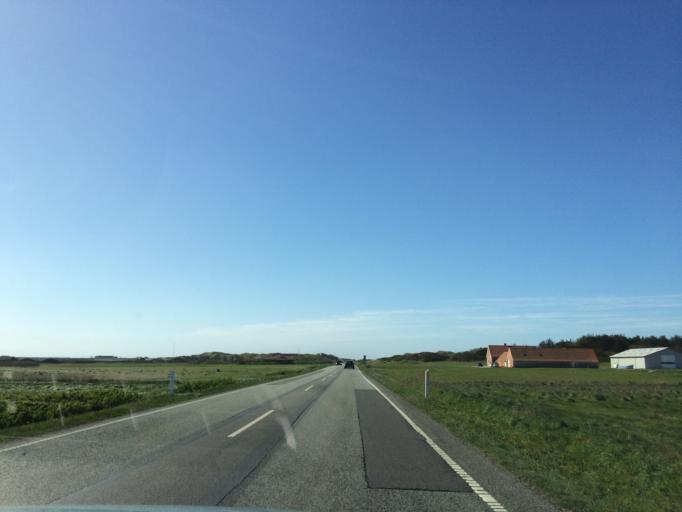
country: DK
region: Central Jutland
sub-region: Ringkobing-Skjern Kommune
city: Hvide Sande
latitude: 55.9652
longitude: 8.1454
